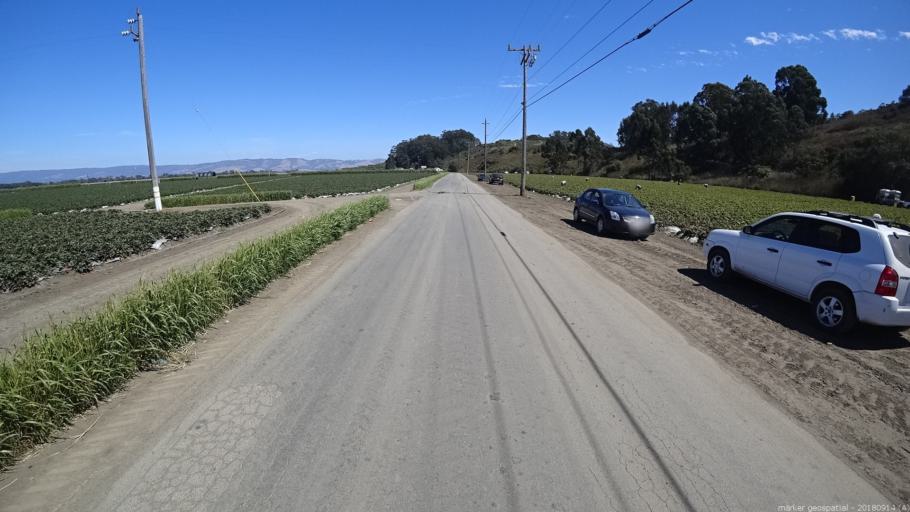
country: US
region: California
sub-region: Santa Cruz County
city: Watsonville
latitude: 36.8677
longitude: -121.7915
